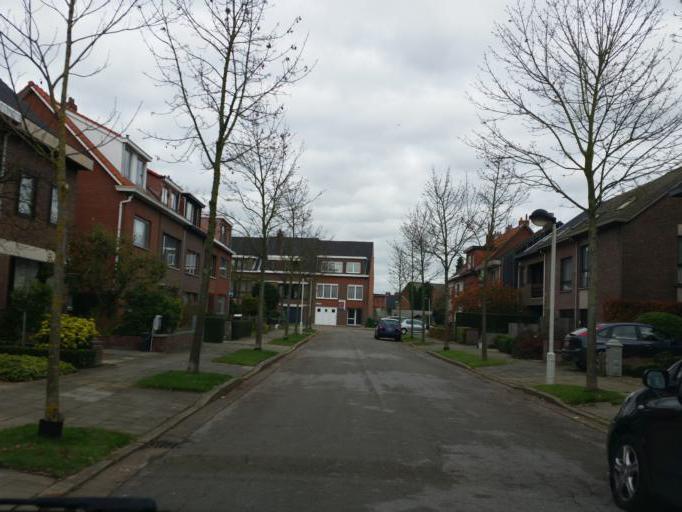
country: BE
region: Flanders
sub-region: Provincie Antwerpen
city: Edegem
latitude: 51.1646
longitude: 4.4427
